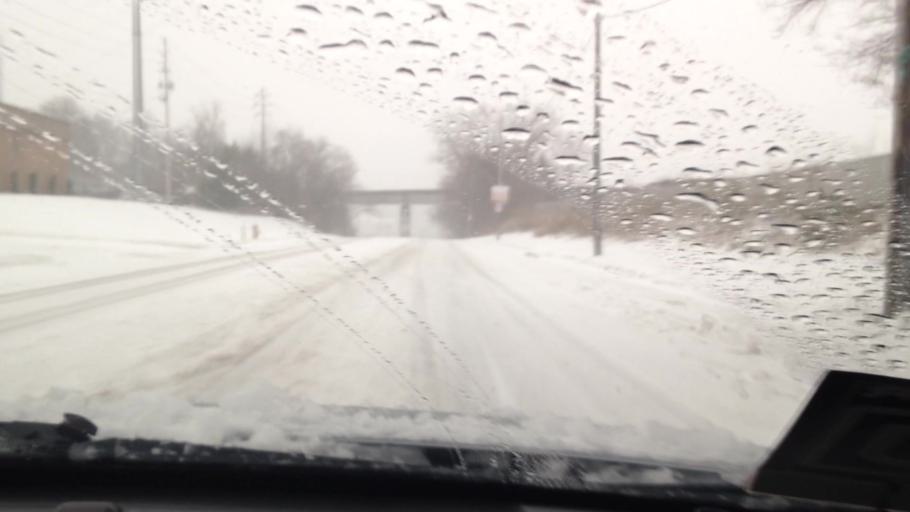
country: US
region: Missouri
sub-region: Jackson County
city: Raytown
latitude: 39.0598
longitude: -94.5017
